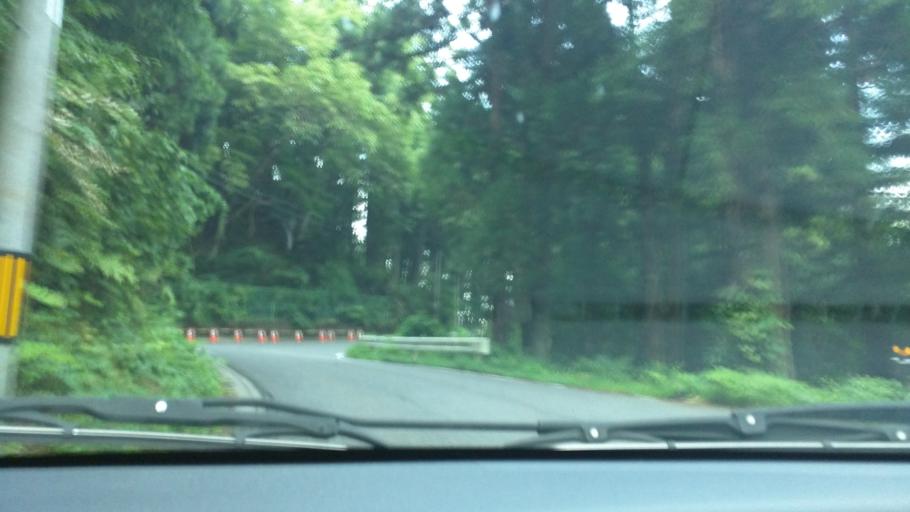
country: JP
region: Fukushima
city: Kitakata
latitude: 37.4841
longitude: 139.6910
